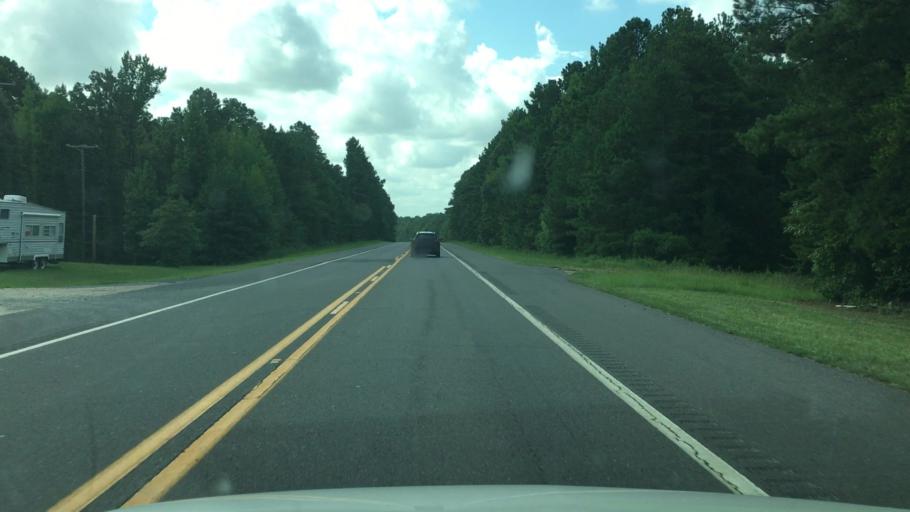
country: US
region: Arkansas
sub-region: Clark County
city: Arkadelphia
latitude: 34.2057
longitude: -93.0789
